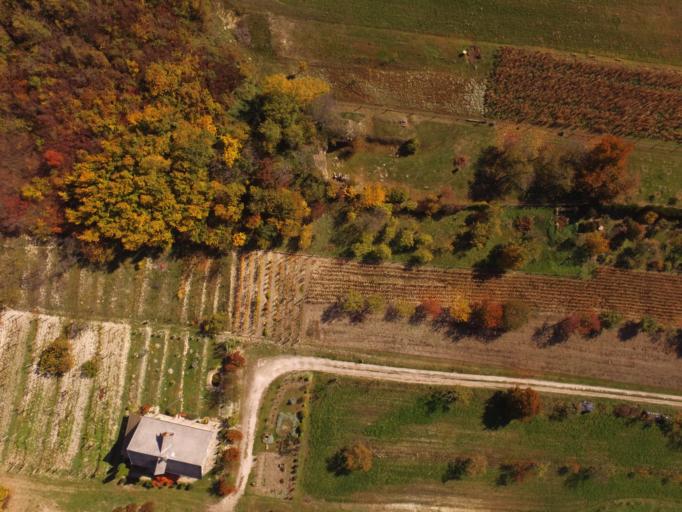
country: HU
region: Fejer
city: Many
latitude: 47.5185
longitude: 18.6211
